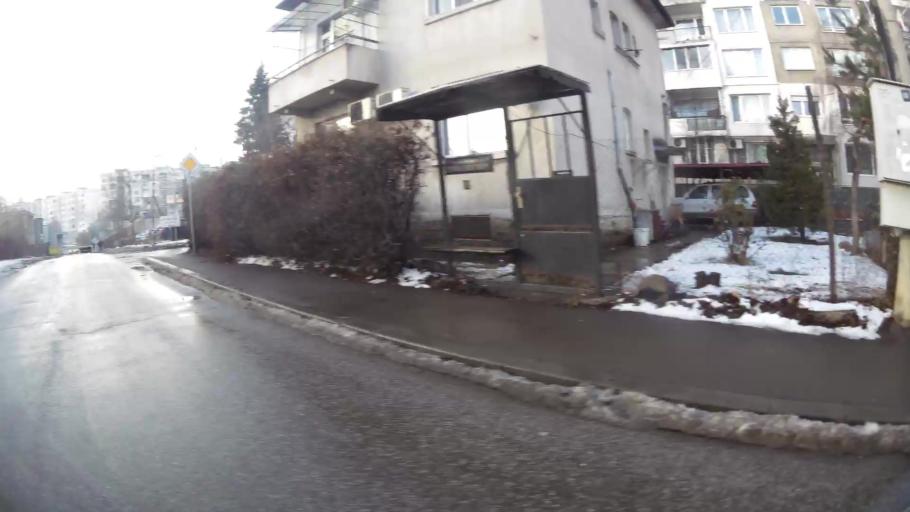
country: BG
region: Sofia-Capital
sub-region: Stolichna Obshtina
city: Sofia
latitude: 42.6977
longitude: 23.2802
